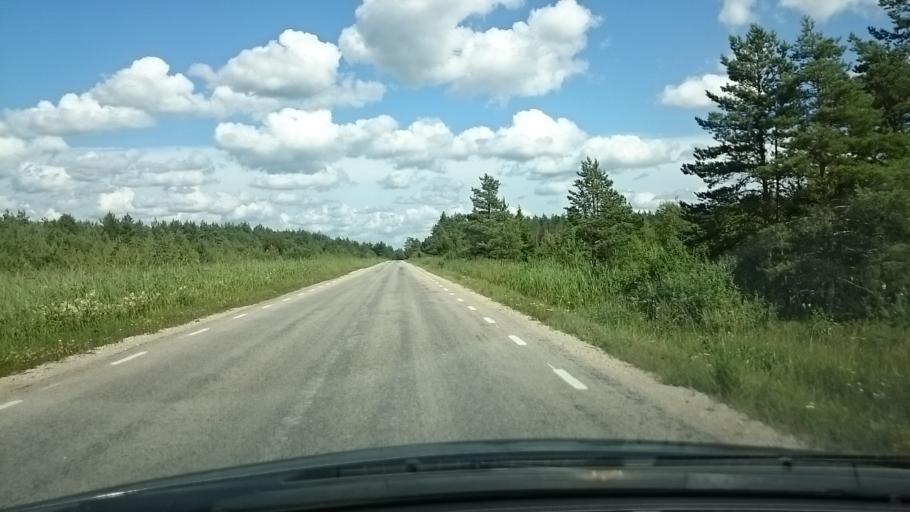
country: EE
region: Laeaene
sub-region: Haapsalu linn
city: Haapsalu
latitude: 59.0501
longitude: 23.5237
